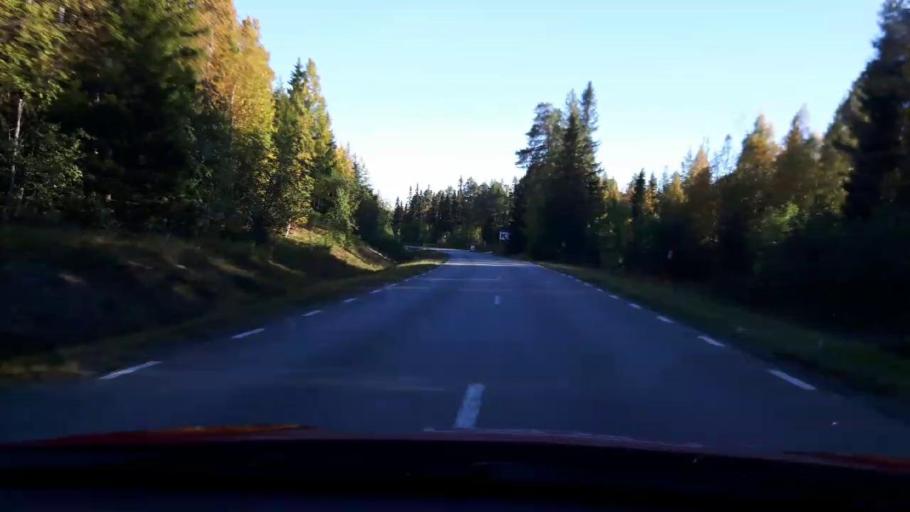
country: SE
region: Jaemtland
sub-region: OEstersunds Kommun
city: Lit
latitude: 63.7524
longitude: 14.7154
